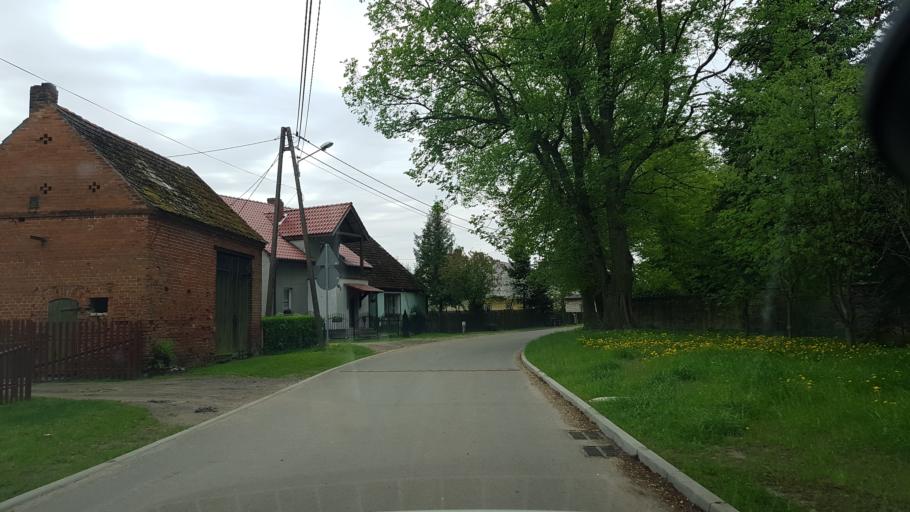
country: PL
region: West Pomeranian Voivodeship
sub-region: Powiat mysliborski
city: Debno
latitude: 52.7078
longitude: 14.6494
